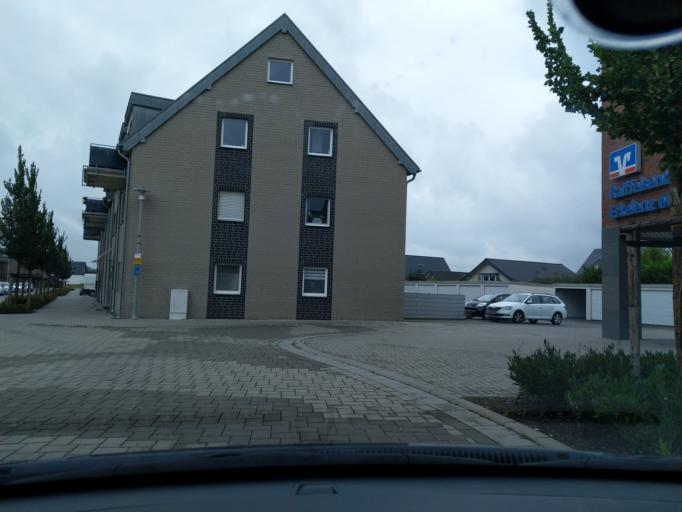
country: DE
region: North Rhine-Westphalia
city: Erkelenz
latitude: 51.0591
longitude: 6.3369
